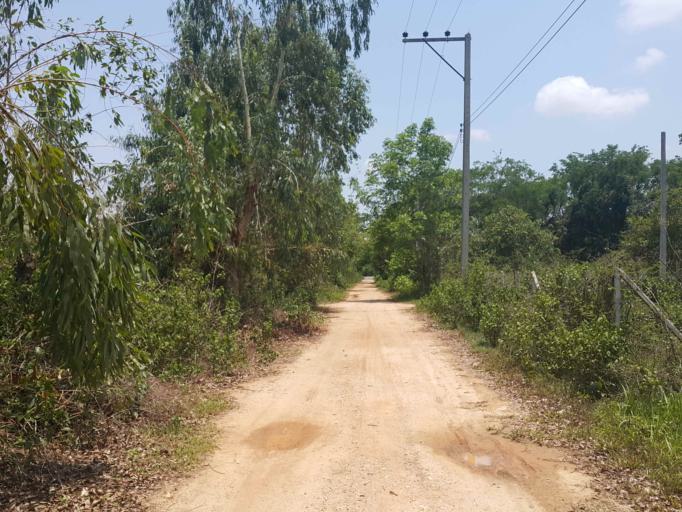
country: TH
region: Chiang Mai
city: San Sai
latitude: 18.8102
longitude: 99.0828
